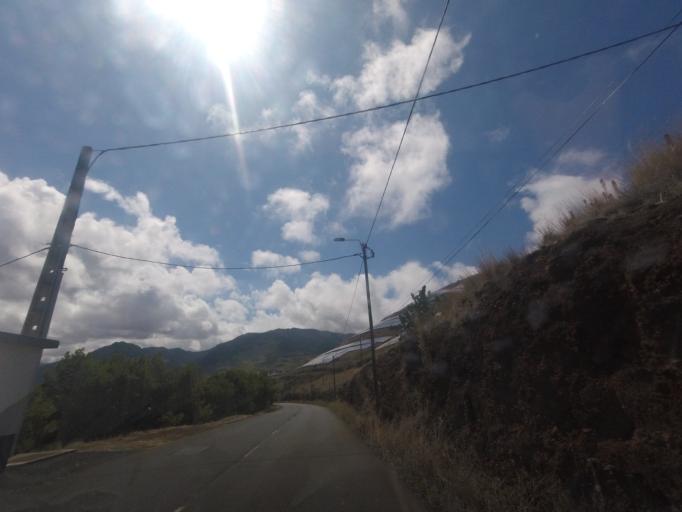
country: PT
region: Madeira
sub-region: Machico
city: Canical
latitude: 32.7438
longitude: -16.7249
